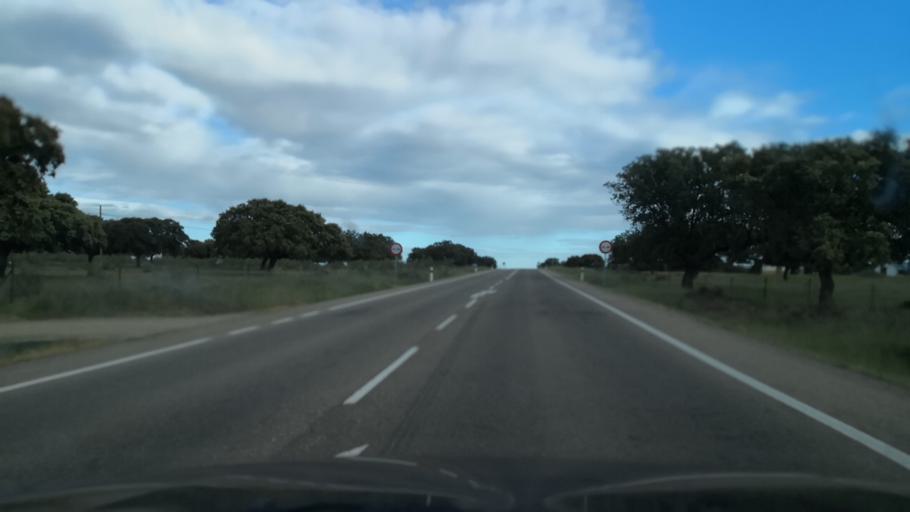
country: ES
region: Extremadura
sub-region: Provincia de Caceres
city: Torrejoncillo
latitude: 39.9239
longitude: -6.4972
